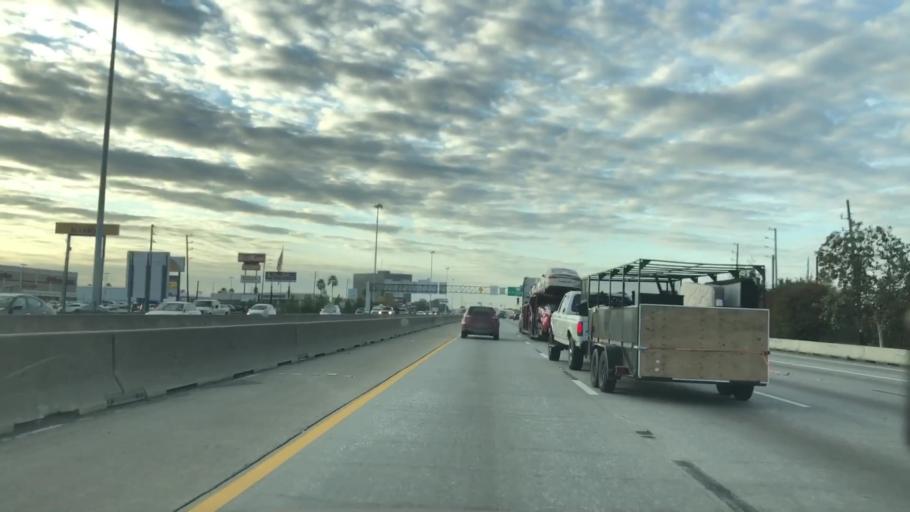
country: US
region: Texas
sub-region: Harris County
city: Aldine
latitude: 29.9289
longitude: -95.4120
